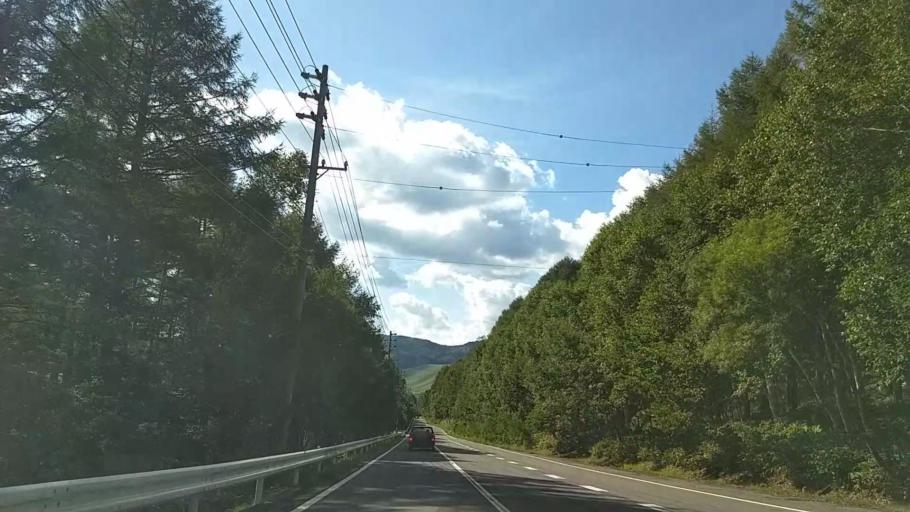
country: JP
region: Nagano
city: Chino
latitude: 36.0990
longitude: 138.2572
